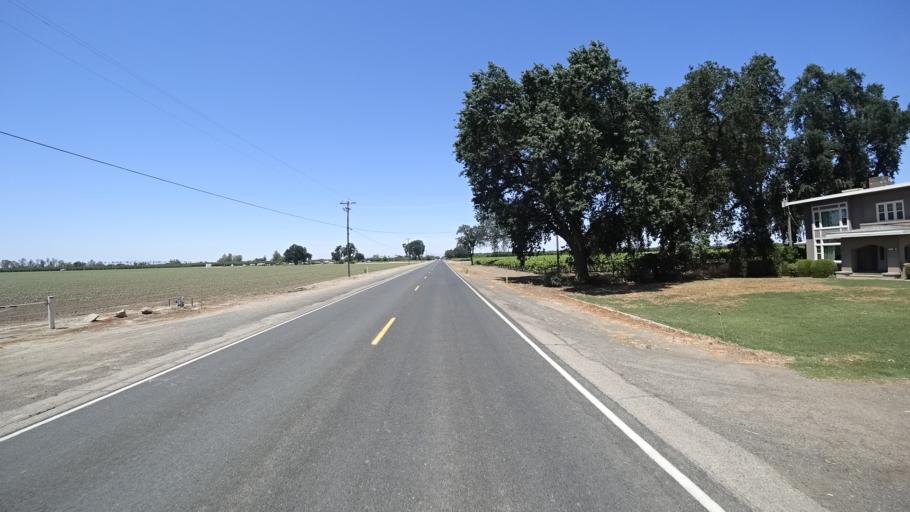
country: US
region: California
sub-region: Kings County
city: Lemoore
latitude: 36.3425
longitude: -119.7968
